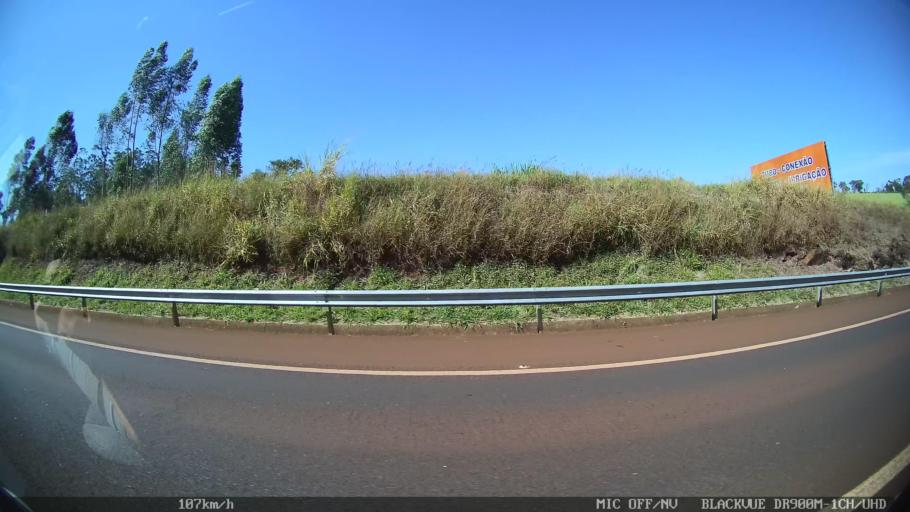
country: BR
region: Sao Paulo
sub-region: Franca
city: Franca
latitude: -20.6280
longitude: -47.4643
